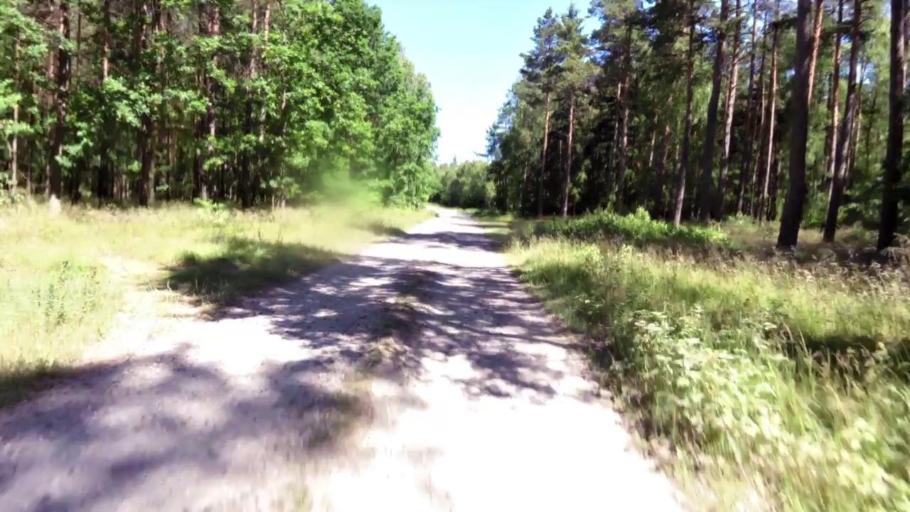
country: PL
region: West Pomeranian Voivodeship
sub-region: Powiat swidwinski
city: Rabino
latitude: 53.8899
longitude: 16.0485
